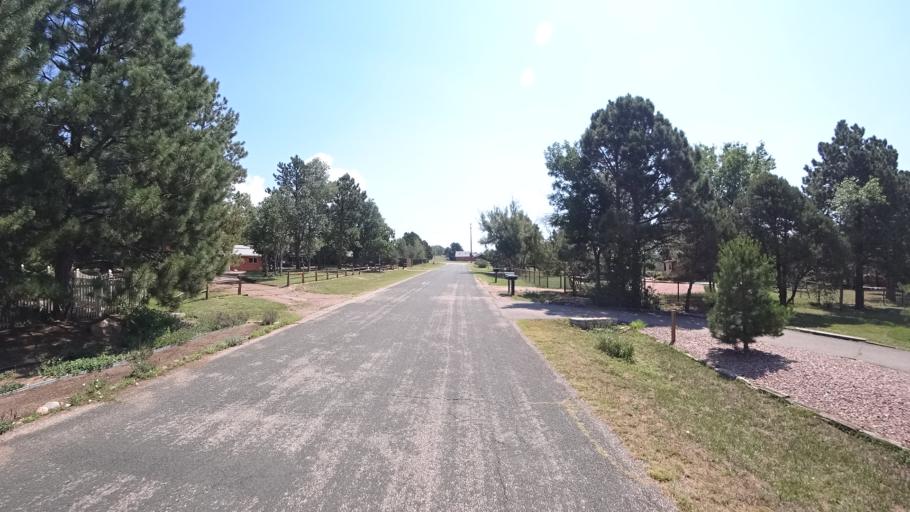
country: US
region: Colorado
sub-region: El Paso County
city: Air Force Academy
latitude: 38.9347
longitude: -104.7863
